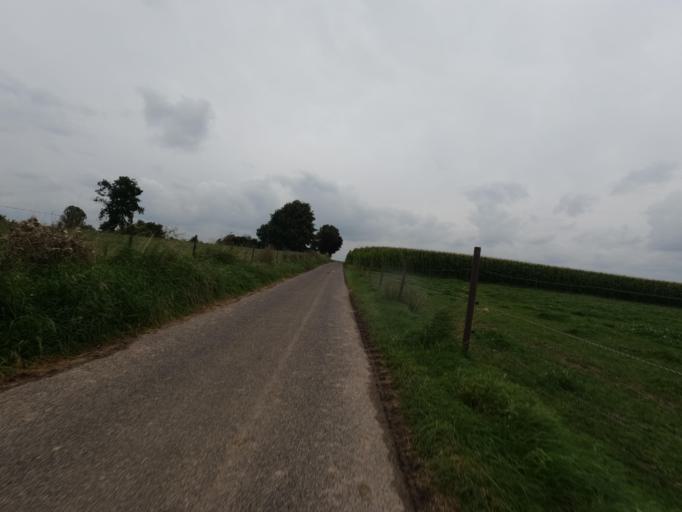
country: DE
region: North Rhine-Westphalia
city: Geilenkirchen
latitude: 50.9713
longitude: 6.1671
